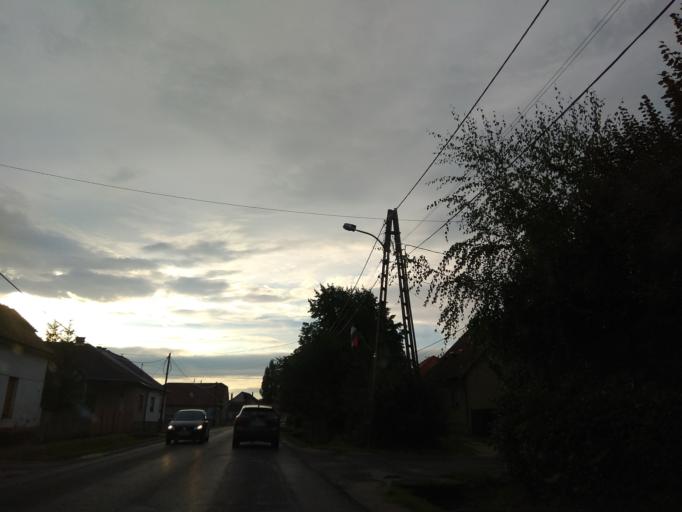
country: HU
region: Borsod-Abauj-Zemplen
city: Miskolc
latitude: 48.0906
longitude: 20.8095
